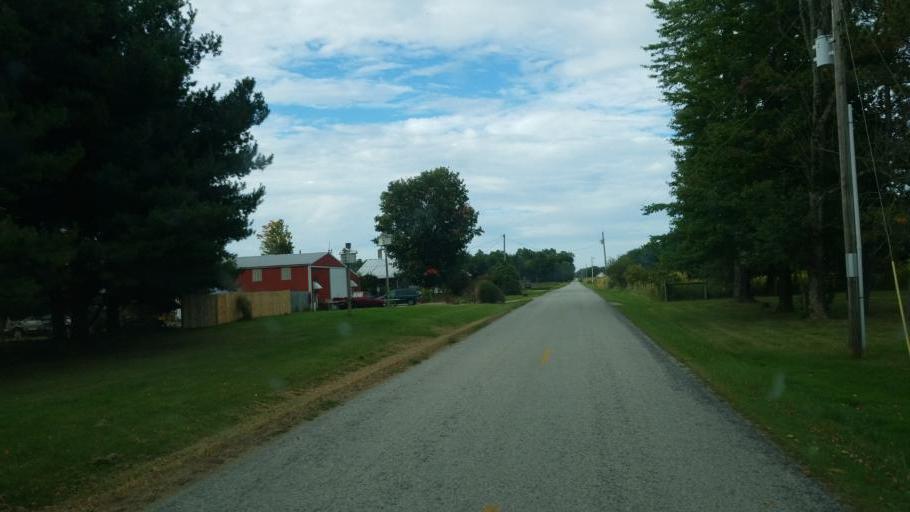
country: US
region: Ohio
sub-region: Knox County
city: Centerburg
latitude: 40.2945
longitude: -82.7733
